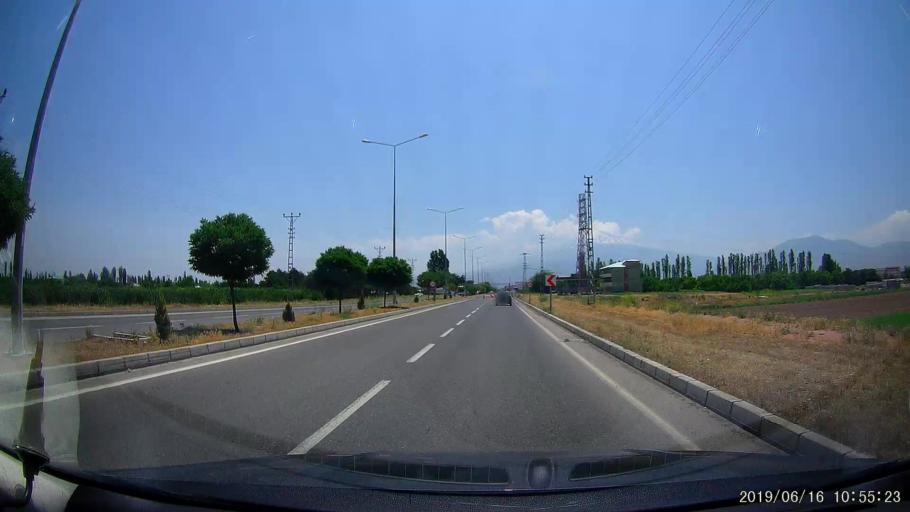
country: TR
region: Igdir
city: Igdir
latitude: 39.9365
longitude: 44.0099
